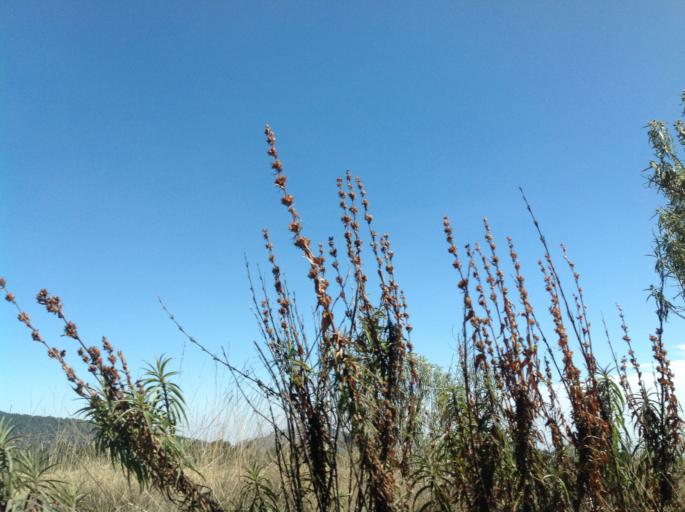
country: MX
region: Mexico
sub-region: Amecameca
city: San Diego Huehuecalco
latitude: 19.1095
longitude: -98.6444
